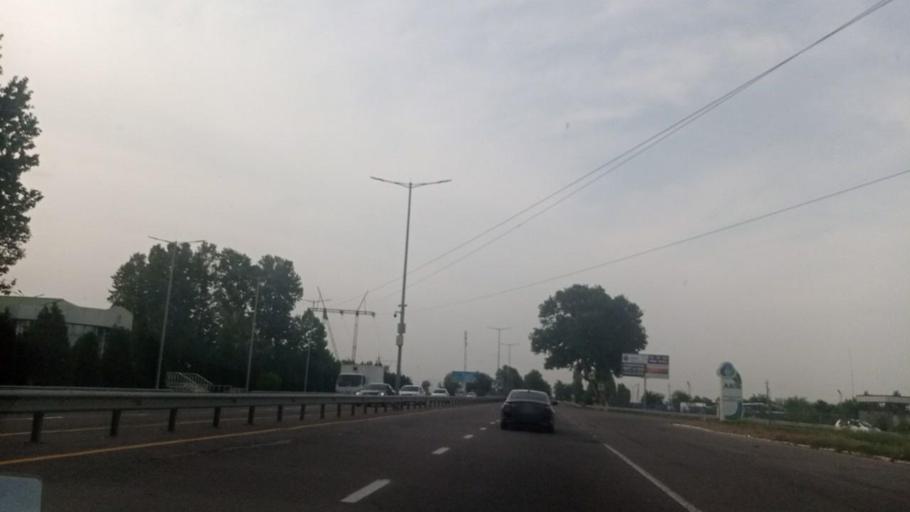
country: UZ
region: Toshkent Shahri
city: Bektemir
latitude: 41.1816
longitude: 69.4067
